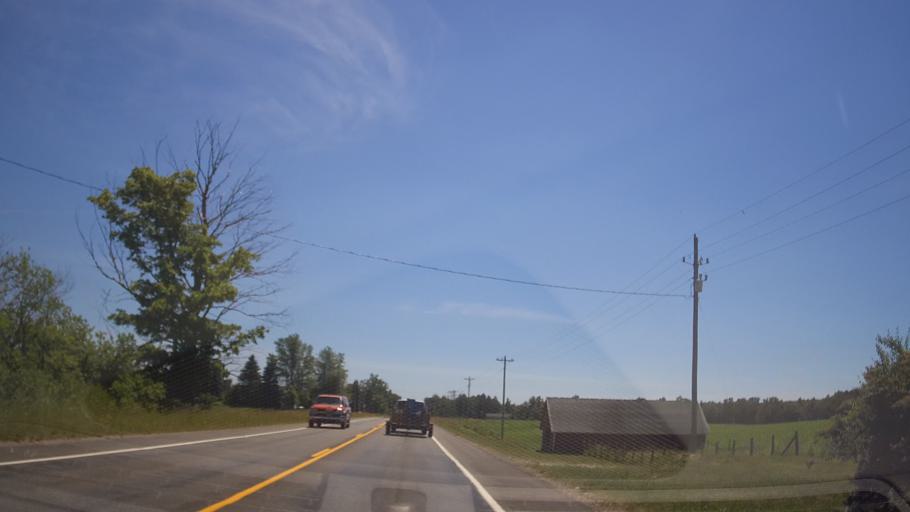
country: US
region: Michigan
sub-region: Grand Traverse County
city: Kingsley
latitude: 44.6021
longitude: -85.6964
